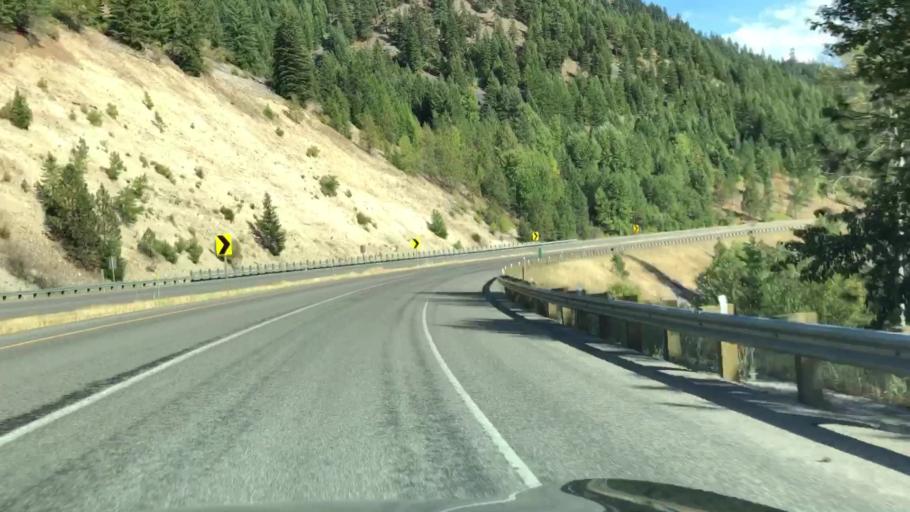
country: US
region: Montana
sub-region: Sanders County
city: Thompson Falls
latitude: 47.3272
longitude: -115.2526
